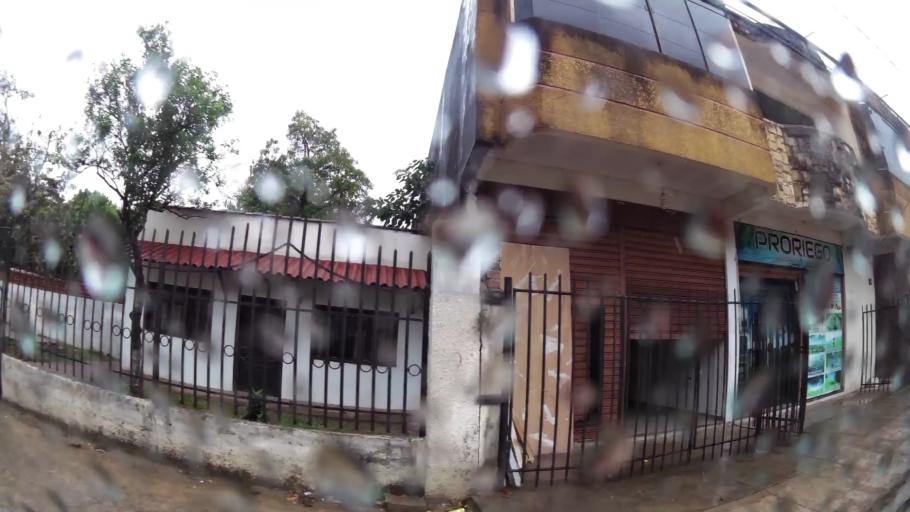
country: BO
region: Santa Cruz
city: Santa Cruz de la Sierra
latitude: -17.7950
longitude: -63.2079
